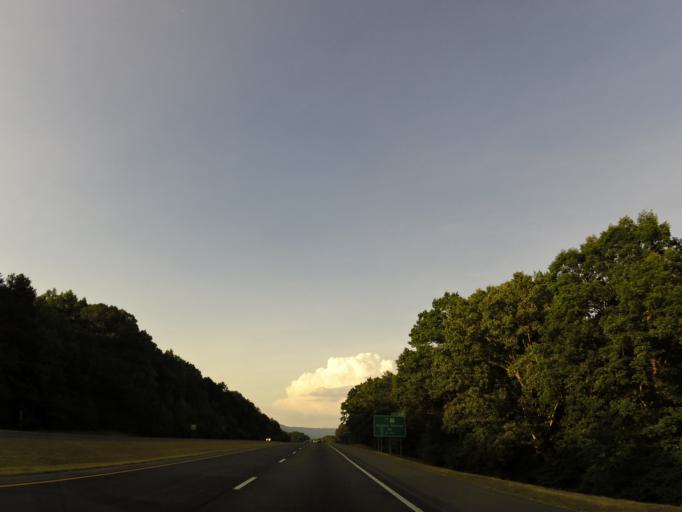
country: US
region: Georgia
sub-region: Dade County
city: Trenton
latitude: 34.6888
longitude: -85.5763
